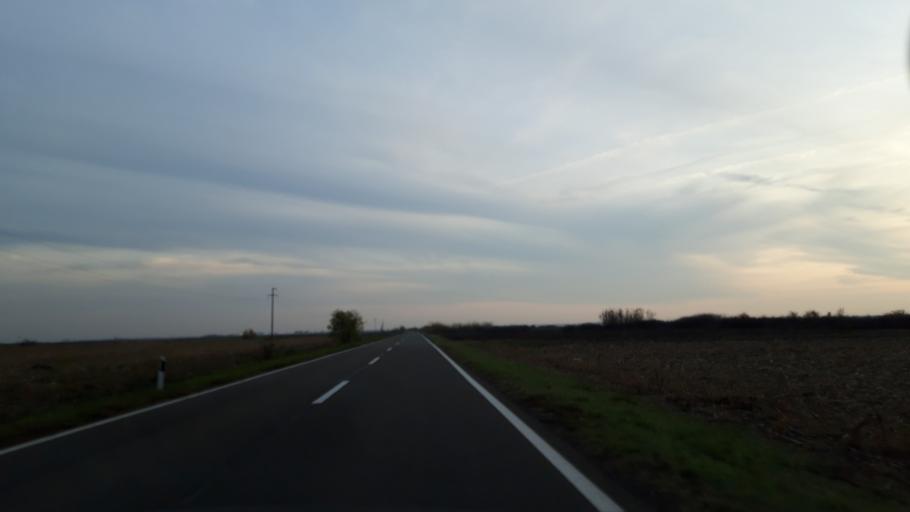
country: RS
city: Ostojicevo
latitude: 45.8683
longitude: 20.1648
